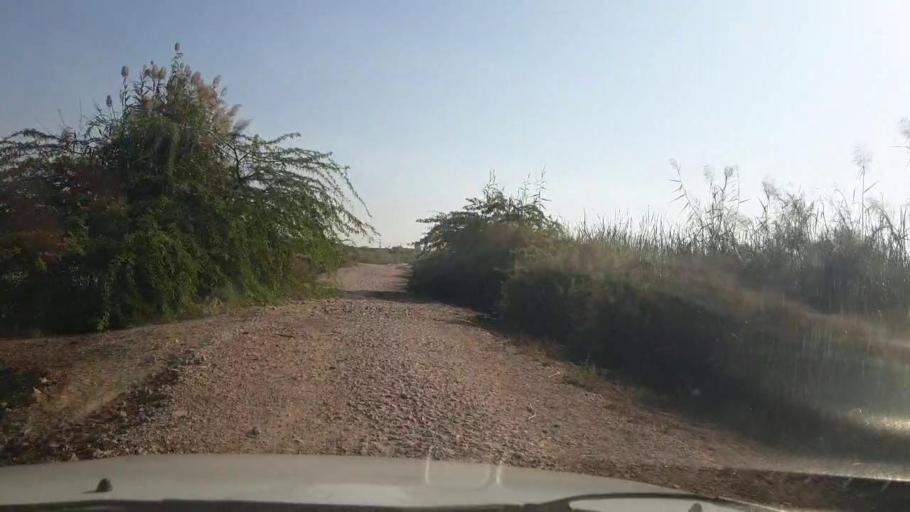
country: PK
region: Sindh
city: Chuhar Jamali
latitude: 24.5548
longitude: 67.9102
